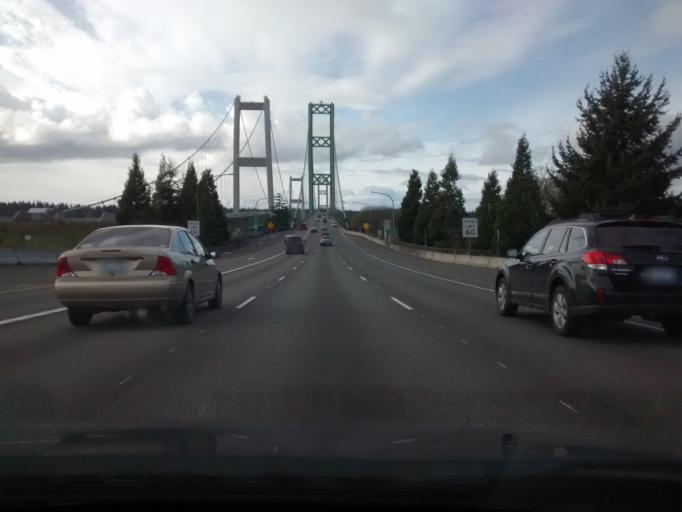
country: US
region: Washington
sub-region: Pierce County
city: University Place
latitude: 47.2615
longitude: -122.5419
